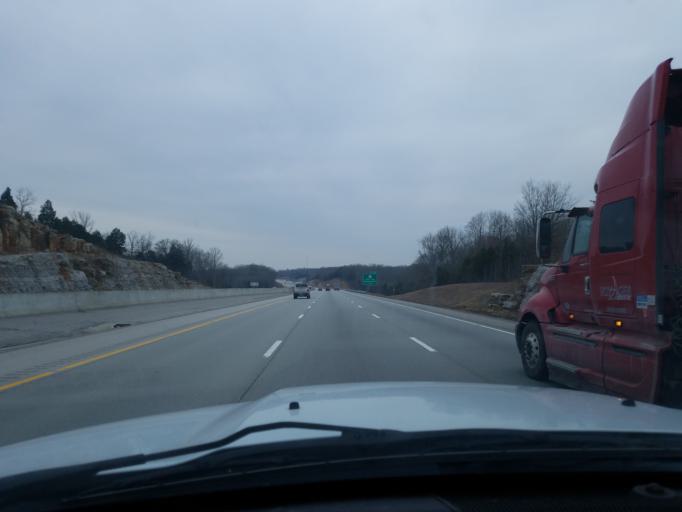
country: US
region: Kentucky
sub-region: Barren County
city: Cave City
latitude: 37.1061
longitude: -86.0424
